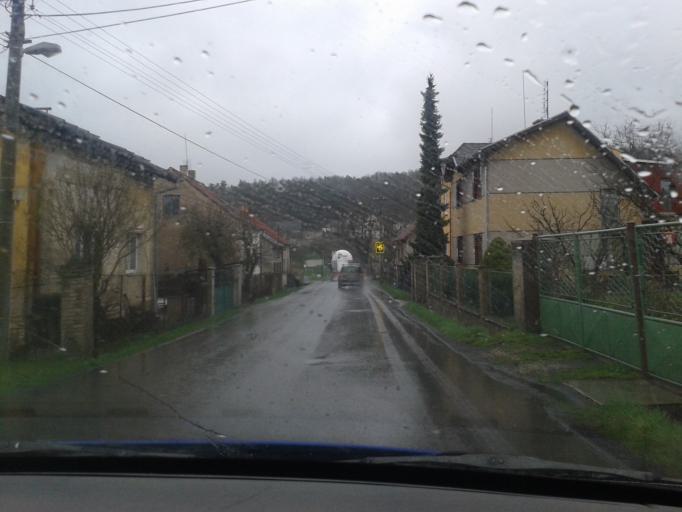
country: CZ
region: Central Bohemia
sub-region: Okres Beroun
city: Kraluv Dvur
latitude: 49.9272
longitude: 14.0379
